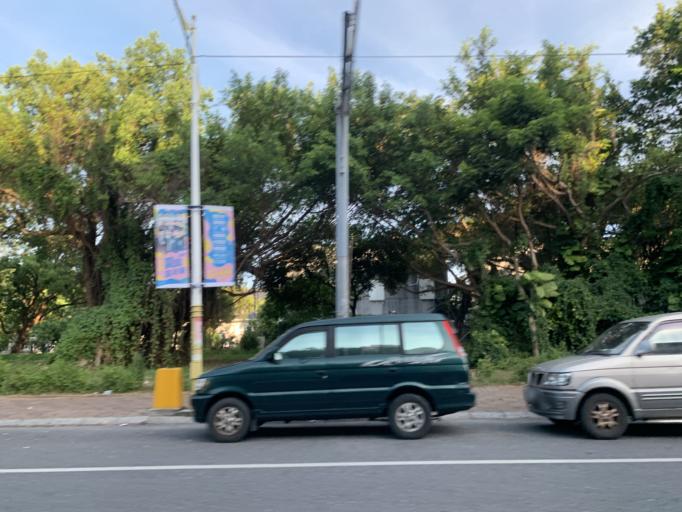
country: TW
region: Taiwan
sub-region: Hualien
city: Hualian
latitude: 23.9887
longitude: 121.6234
